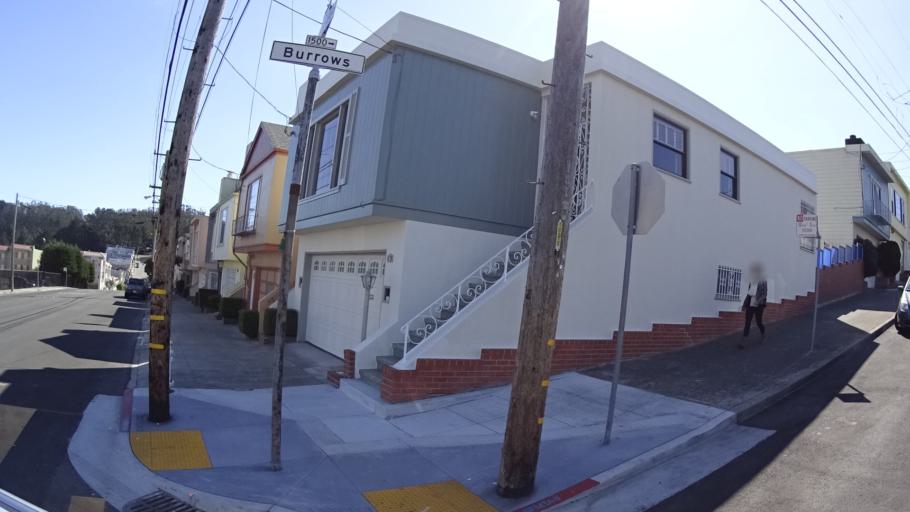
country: US
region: California
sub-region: San Mateo County
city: Brisbane
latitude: 37.7251
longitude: -122.4180
